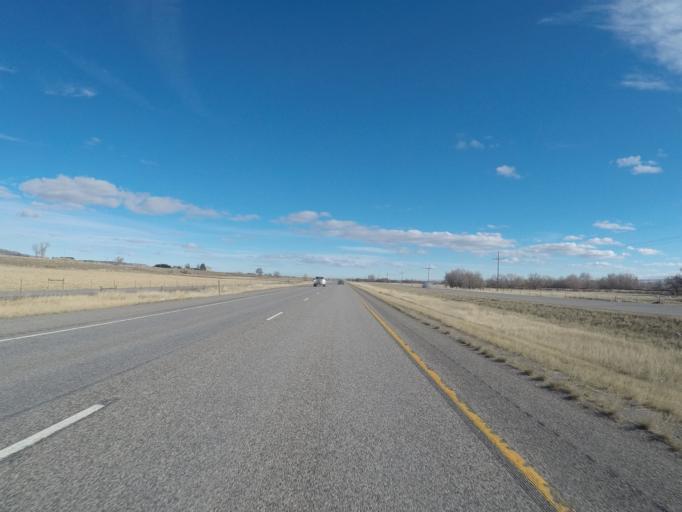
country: US
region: Montana
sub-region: Yellowstone County
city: Laurel
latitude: 45.6444
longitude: -108.8739
